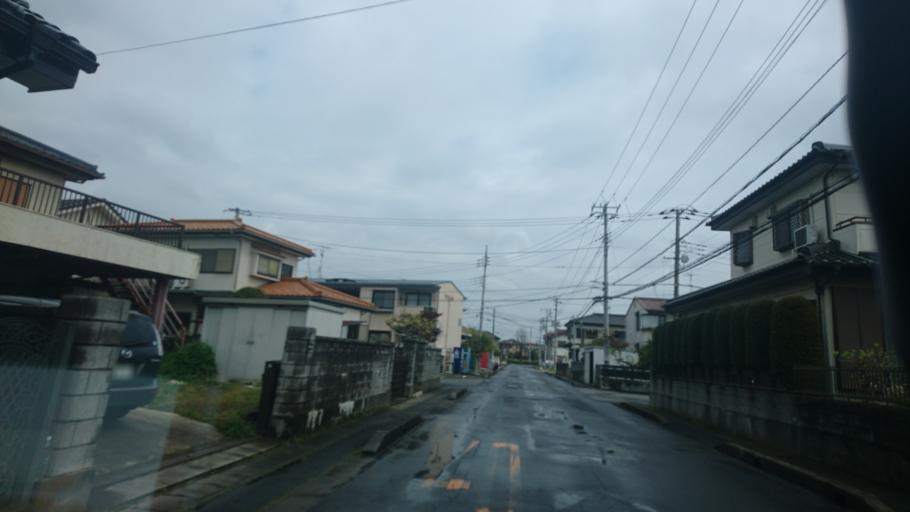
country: JP
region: Ibaraki
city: Mitsukaido
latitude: 36.0127
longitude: 139.9860
